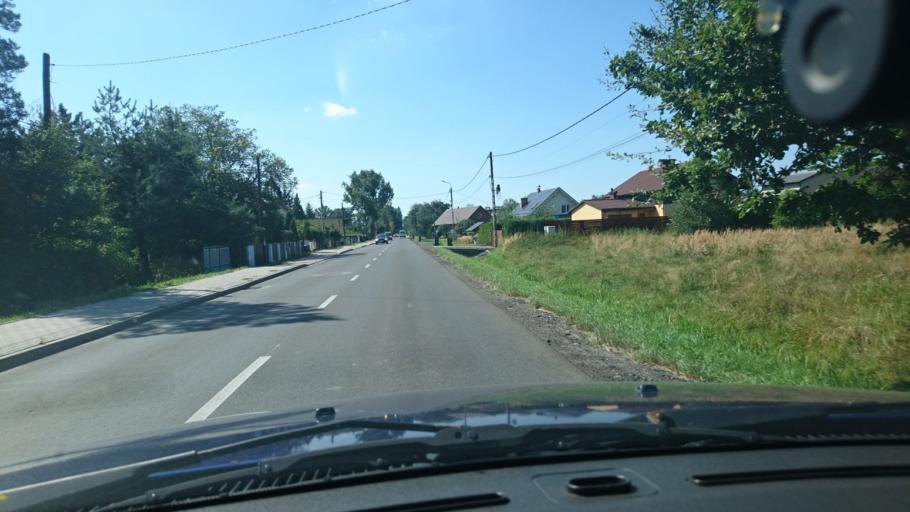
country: PL
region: Silesian Voivodeship
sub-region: Powiat bielski
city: Ligota
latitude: 49.9161
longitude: 18.9678
